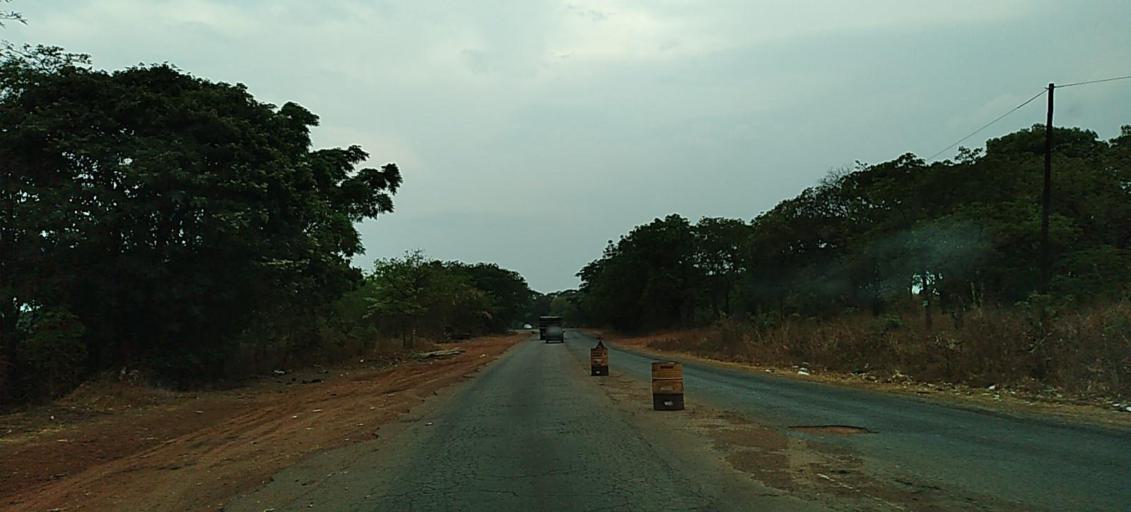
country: ZM
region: Copperbelt
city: Luanshya
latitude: -13.0491
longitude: 28.4651
